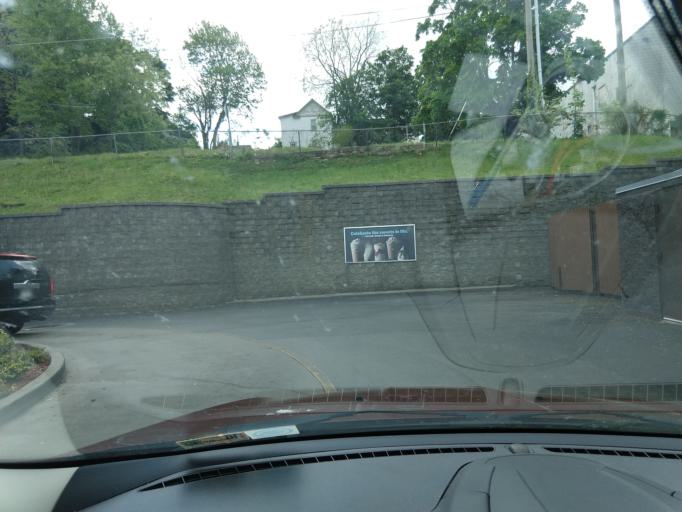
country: US
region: West Virginia
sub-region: Mercer County
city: Bluefield
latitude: 37.2662
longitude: -81.2320
